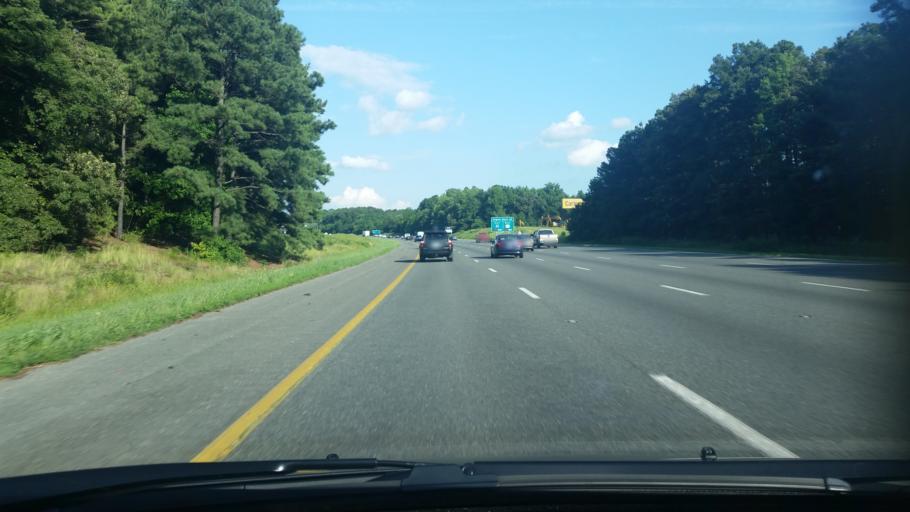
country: US
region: Virginia
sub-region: Henrico County
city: Chamberlayne
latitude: 37.6396
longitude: -77.4078
